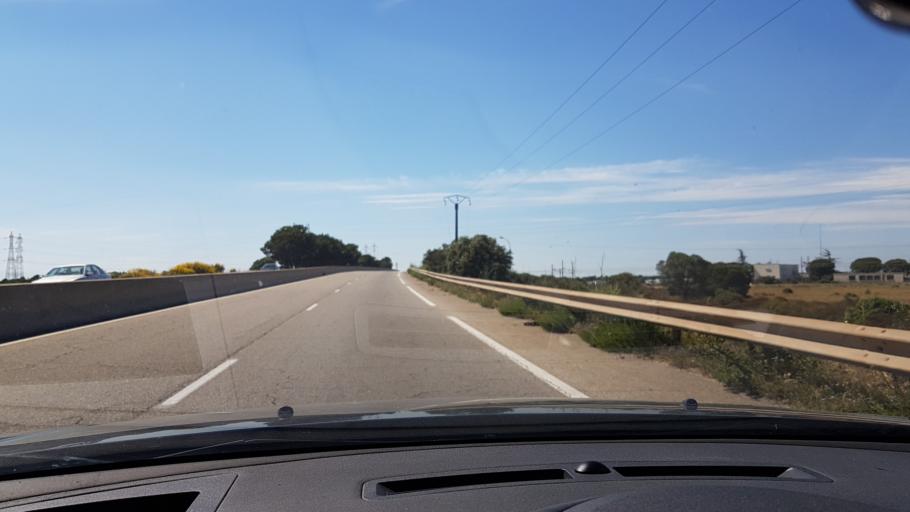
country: FR
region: Provence-Alpes-Cote d'Azur
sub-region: Departement des Bouches-du-Rhone
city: Fos-sur-Mer
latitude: 43.4723
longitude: 4.9060
